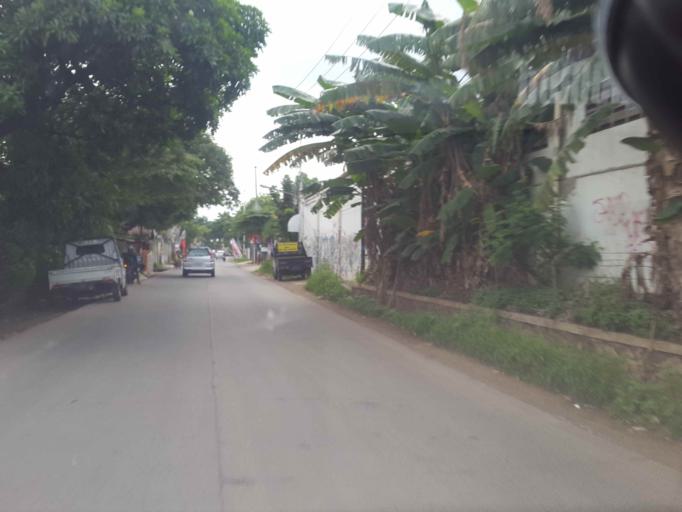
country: ID
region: West Java
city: Bekasi
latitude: -6.3092
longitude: 106.9537
